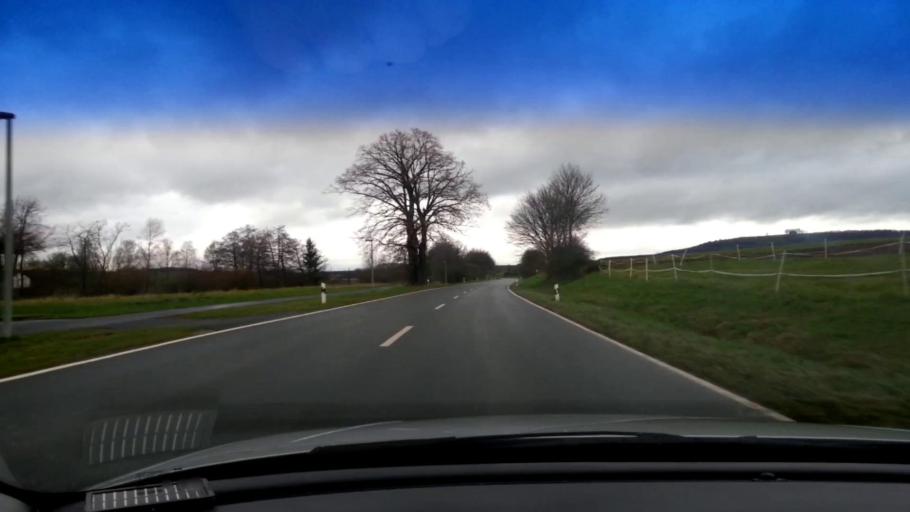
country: DE
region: Bavaria
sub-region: Upper Franconia
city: Ebensfeld
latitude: 50.0370
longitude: 11.0017
